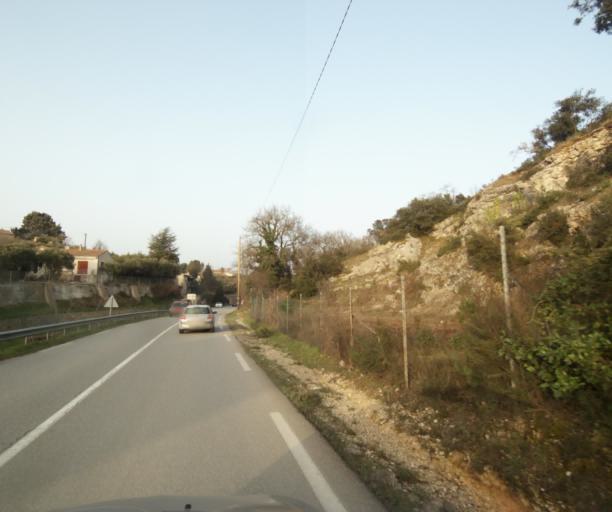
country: FR
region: Provence-Alpes-Cote d'Azur
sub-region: Departement des Bouches-du-Rhone
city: Rognes
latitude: 43.6645
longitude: 5.3497
